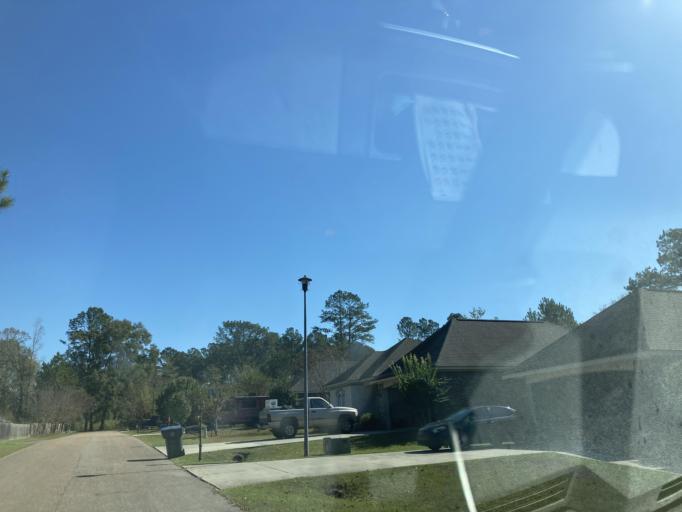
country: US
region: Mississippi
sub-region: Lamar County
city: Sumrall
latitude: 31.3080
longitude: -89.4947
